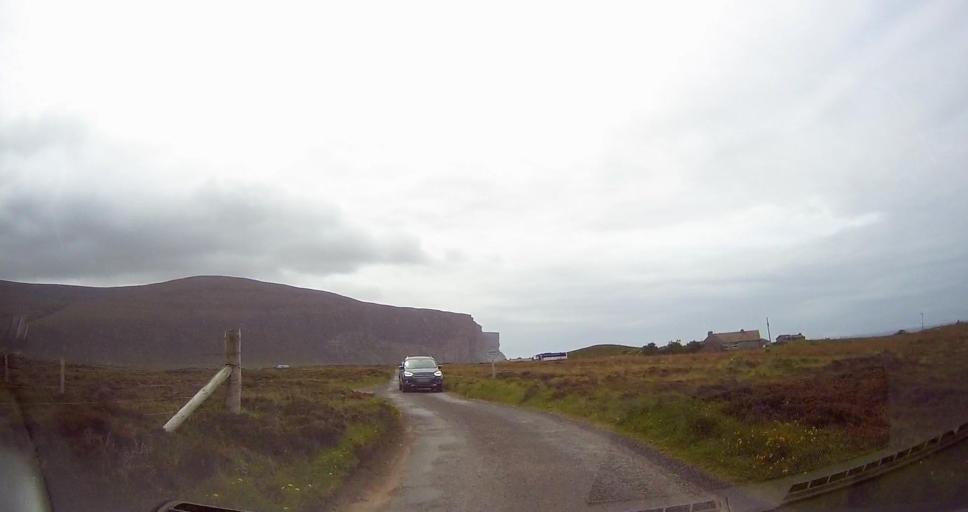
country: GB
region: Scotland
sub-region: Orkney Islands
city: Stromness
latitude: 58.8752
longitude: -3.3867
